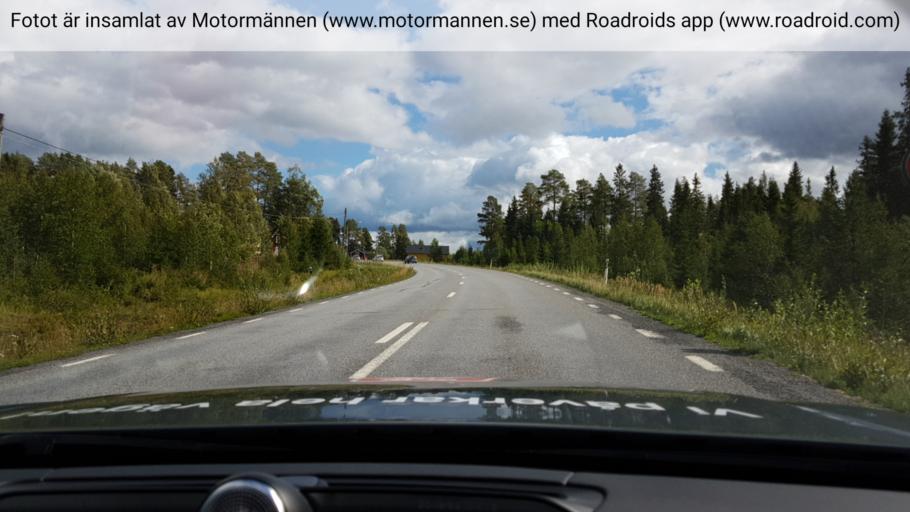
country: SE
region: Jaemtland
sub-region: OEstersunds Kommun
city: Lit
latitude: 63.3896
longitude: 14.9374
